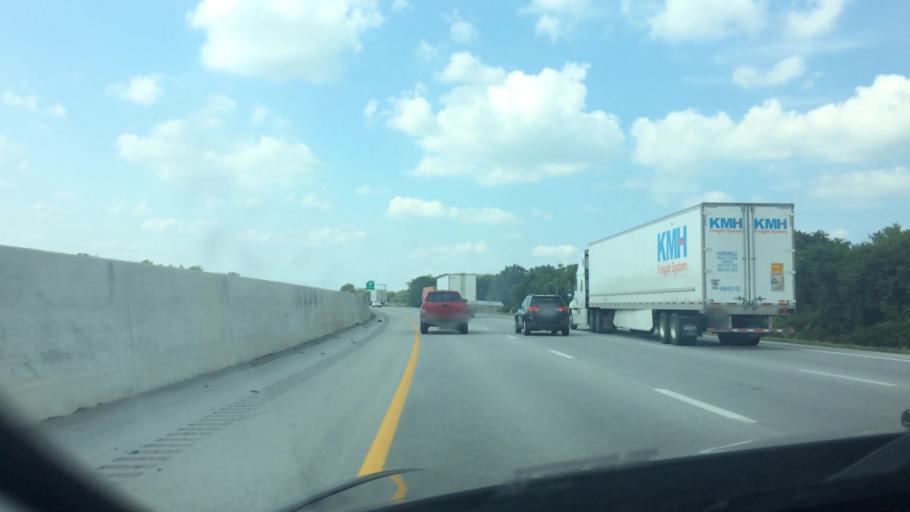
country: US
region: Ohio
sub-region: Wood County
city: North Baltimore
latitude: 41.2174
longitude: -83.6496
